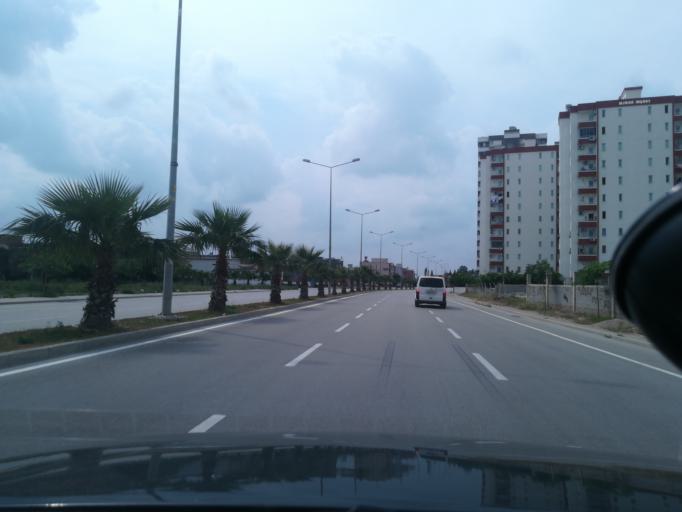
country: TR
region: Adana
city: Seyhan
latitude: 37.0044
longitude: 35.2583
